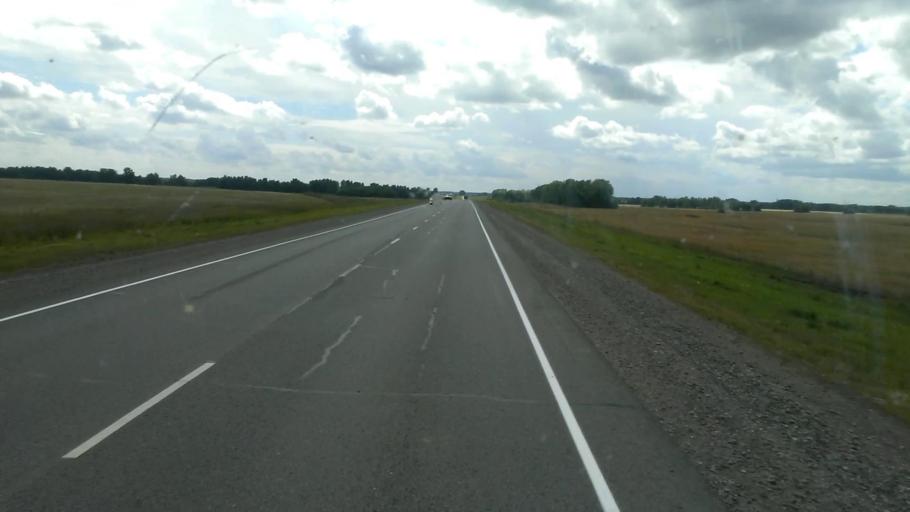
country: RU
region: Altai Krai
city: Troitskoye
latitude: 52.8962
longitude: 84.8344
